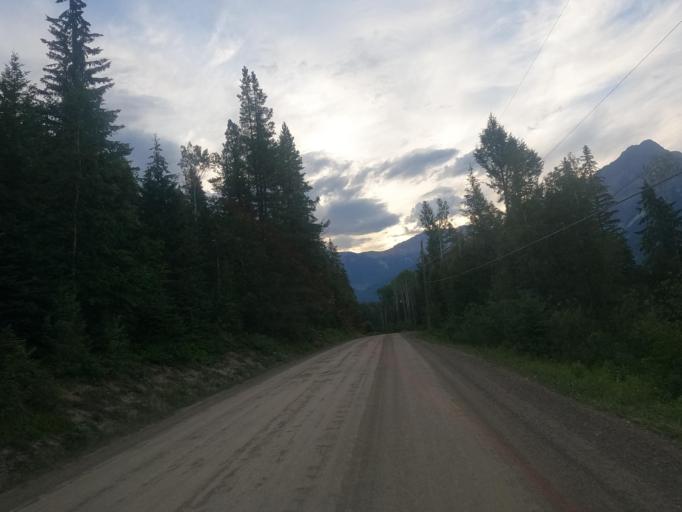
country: CA
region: British Columbia
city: Golden
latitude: 51.4445
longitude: -117.0275
